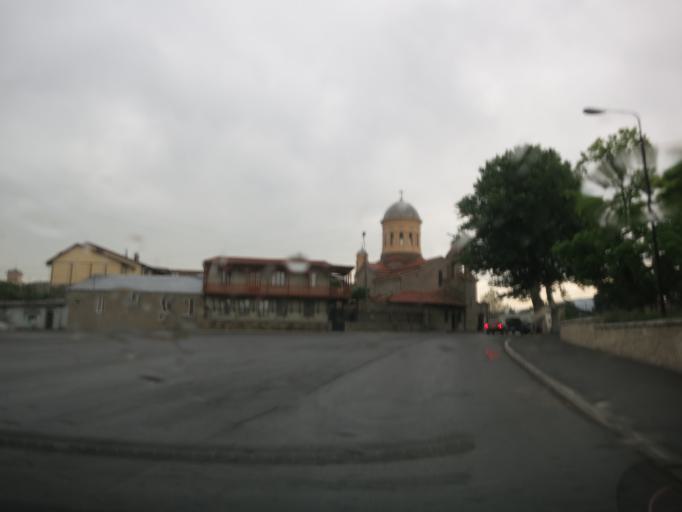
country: GE
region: Shida Kartli
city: Gori
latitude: 41.9870
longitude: 44.1094
